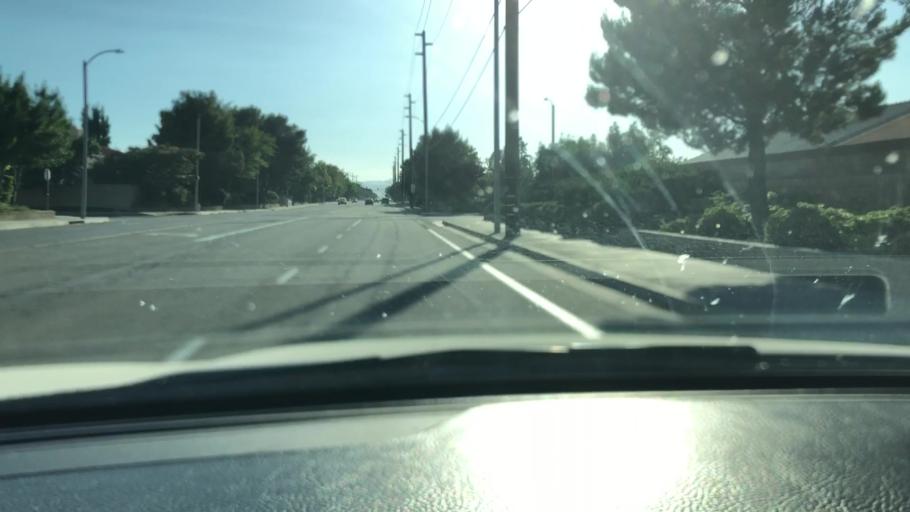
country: US
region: California
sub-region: Los Angeles County
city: Lancaster
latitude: 34.6823
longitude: -118.1695
